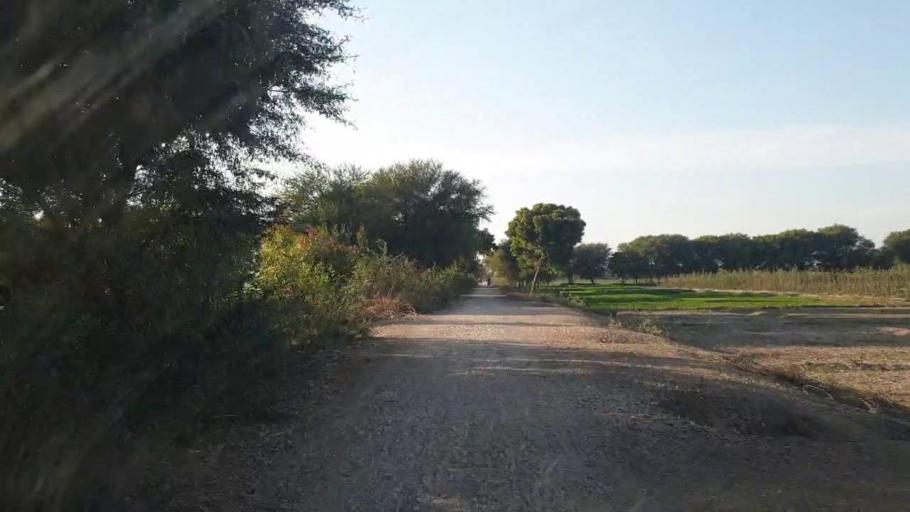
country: PK
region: Sindh
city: Chambar
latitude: 25.2811
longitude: 68.8044
